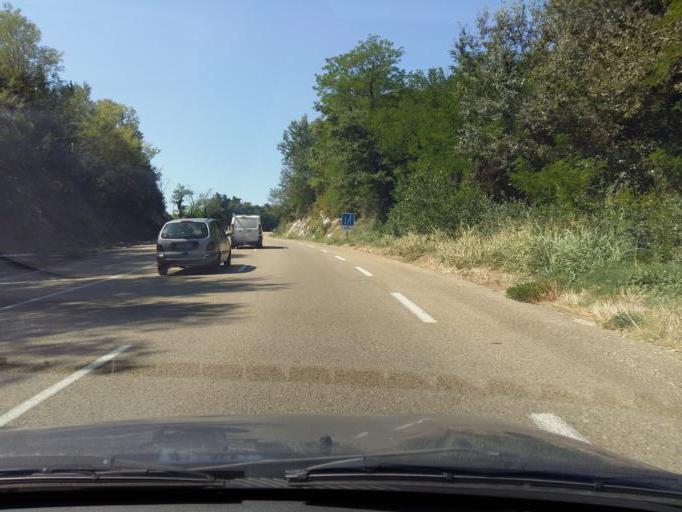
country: FR
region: Languedoc-Roussillon
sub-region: Departement du Gard
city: Saze
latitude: 43.9507
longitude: 4.6728
